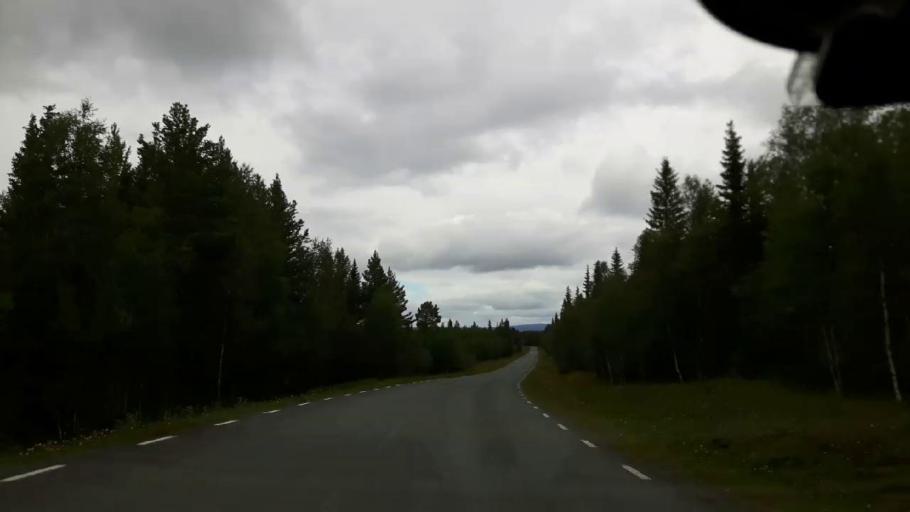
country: SE
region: Jaemtland
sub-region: Krokoms Kommun
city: Valla
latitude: 63.5490
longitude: 13.8500
